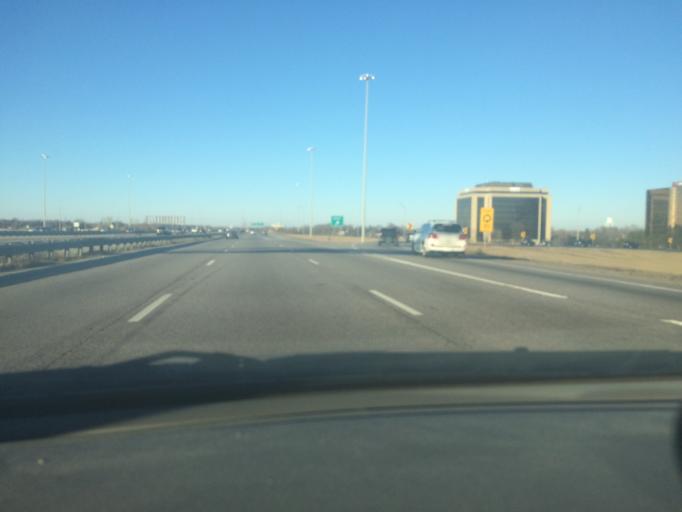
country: US
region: Illinois
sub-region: Cook County
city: Rolling Meadows
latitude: 42.0581
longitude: -88.0281
